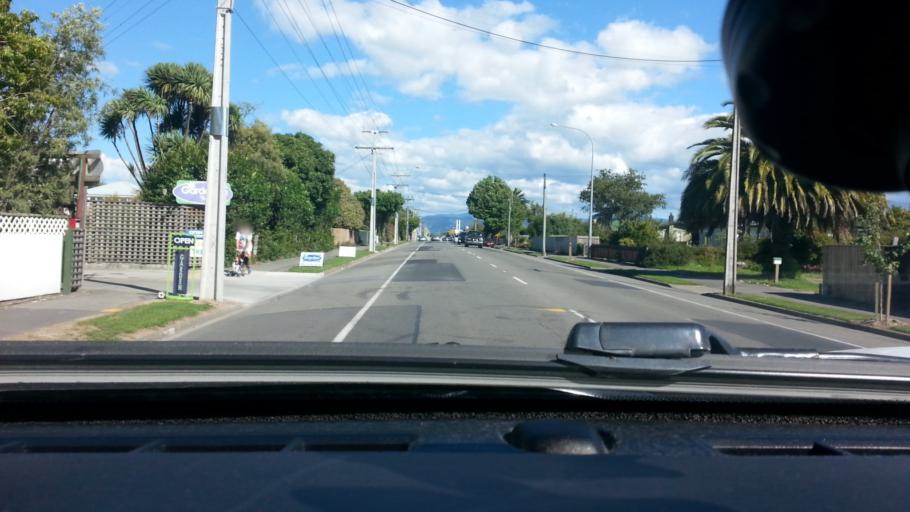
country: NZ
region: Wellington
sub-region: Masterton District
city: Masterton
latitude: -40.9620
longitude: 175.6296
